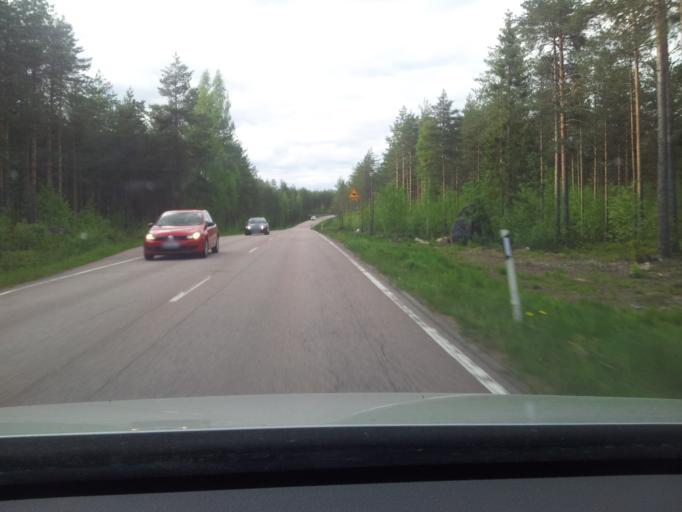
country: FI
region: South Karelia
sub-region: Lappeenranta
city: Luumaeki
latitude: 60.9342
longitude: 27.5833
